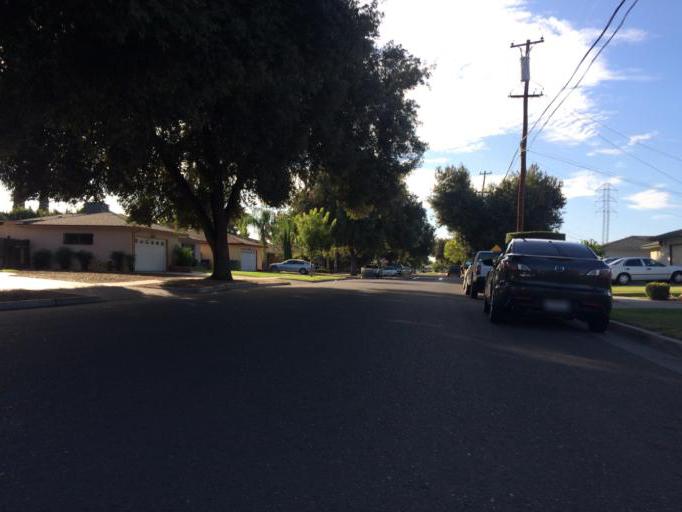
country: US
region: California
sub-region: Fresno County
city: Sunnyside
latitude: 36.7601
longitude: -119.7295
